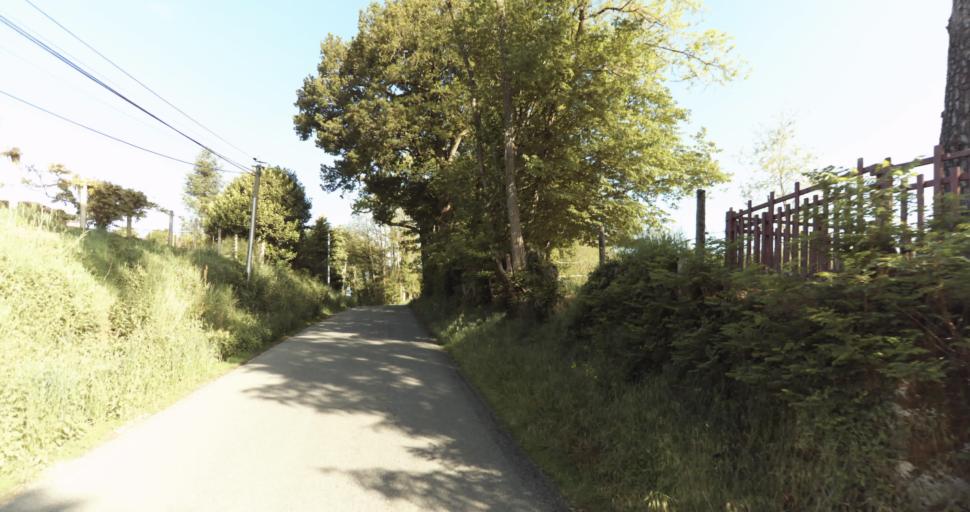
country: FR
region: Limousin
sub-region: Departement de la Haute-Vienne
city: Solignac
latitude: 45.7386
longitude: 1.2748
